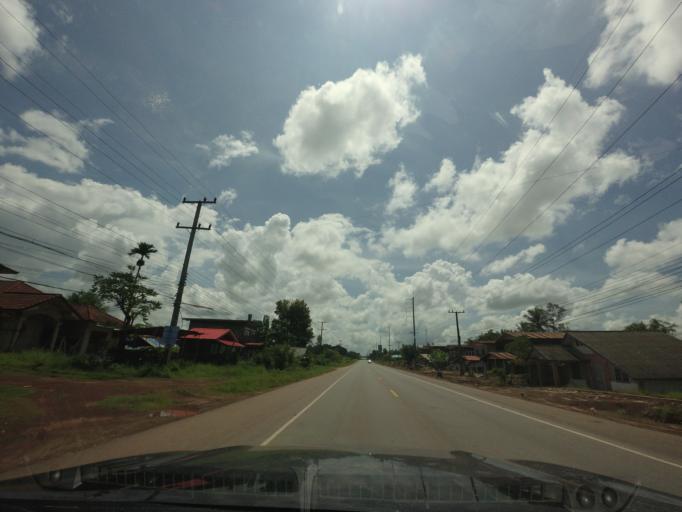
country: TH
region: Changwat Udon Thani
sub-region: Amphoe Ban Phue
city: Ban Phue
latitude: 17.6811
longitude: 102.5036
